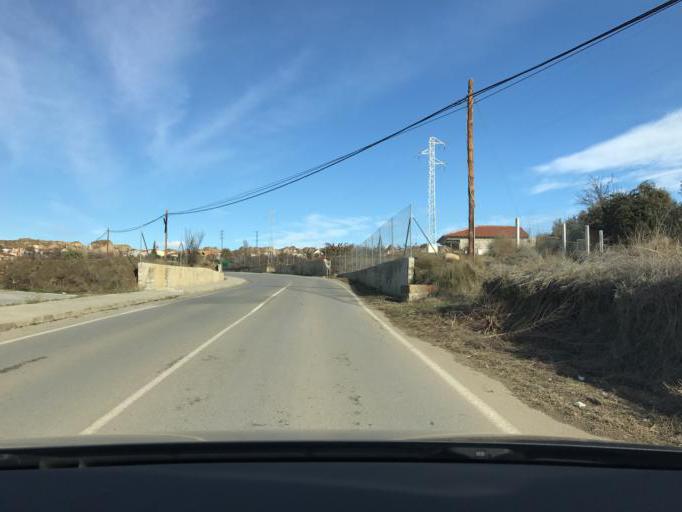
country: ES
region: Andalusia
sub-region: Provincia de Granada
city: Purullena
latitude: 37.3127
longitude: -3.1949
